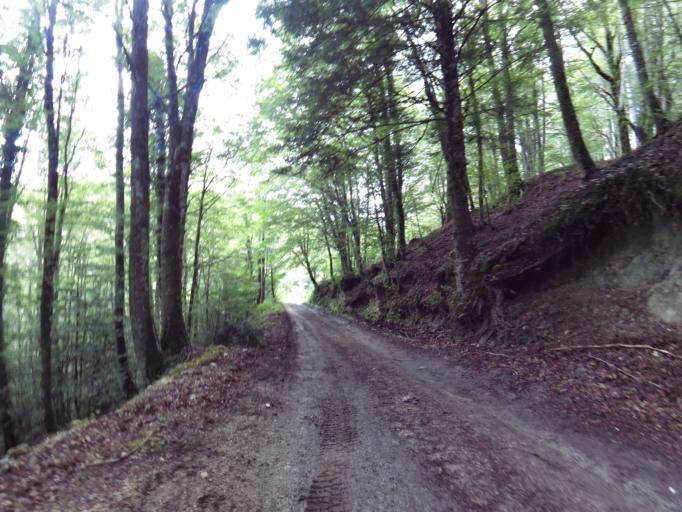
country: IT
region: Calabria
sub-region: Provincia di Vibo-Valentia
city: Nardodipace
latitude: 38.5221
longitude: 16.3837
